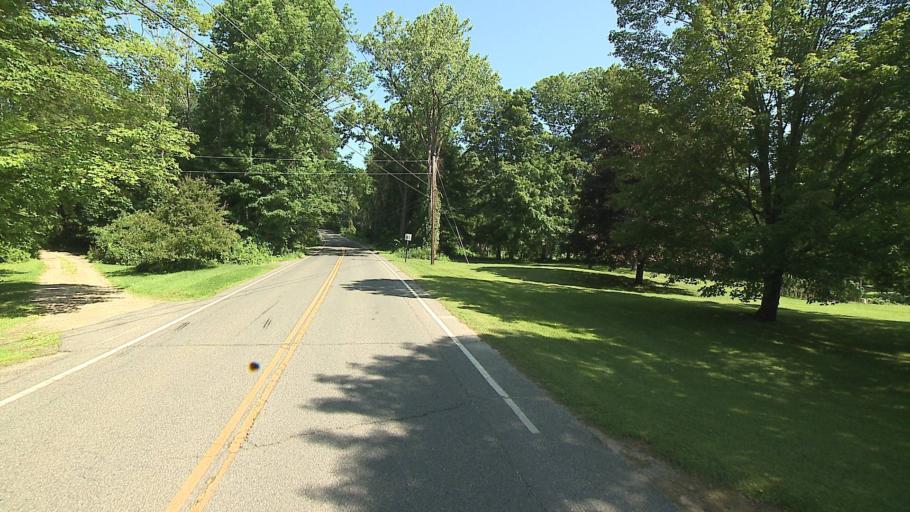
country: US
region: Massachusetts
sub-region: Berkshire County
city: Sheffield
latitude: 42.0449
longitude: -73.4240
